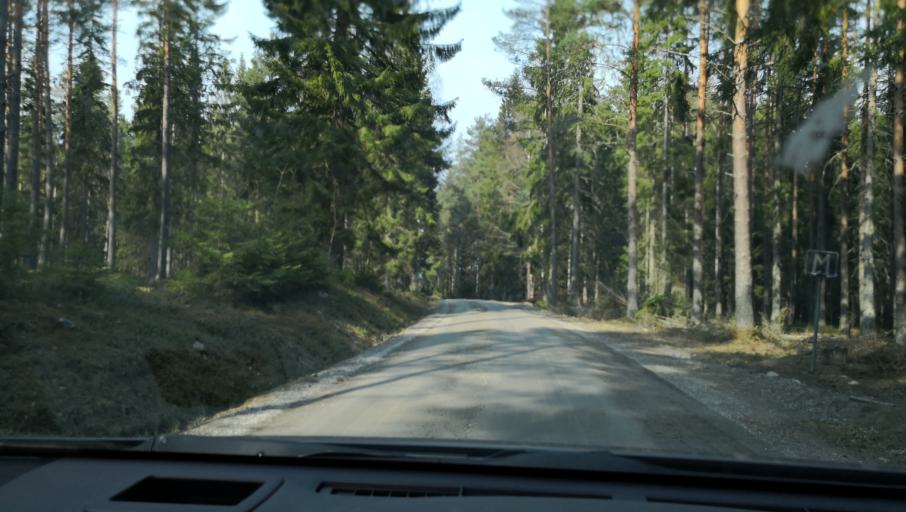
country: SE
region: OErebro
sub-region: Lindesbergs Kommun
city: Frovi
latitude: 59.3583
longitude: 15.4343
